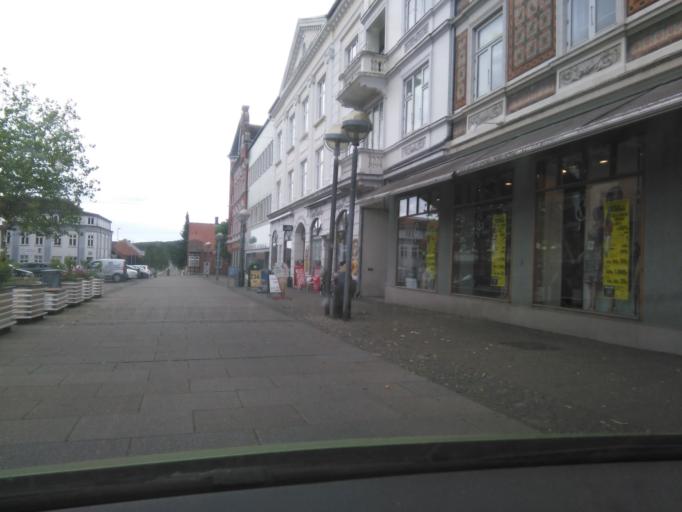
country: DK
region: Central Jutland
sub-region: Odder Kommune
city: Odder
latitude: 55.9723
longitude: 10.1468
